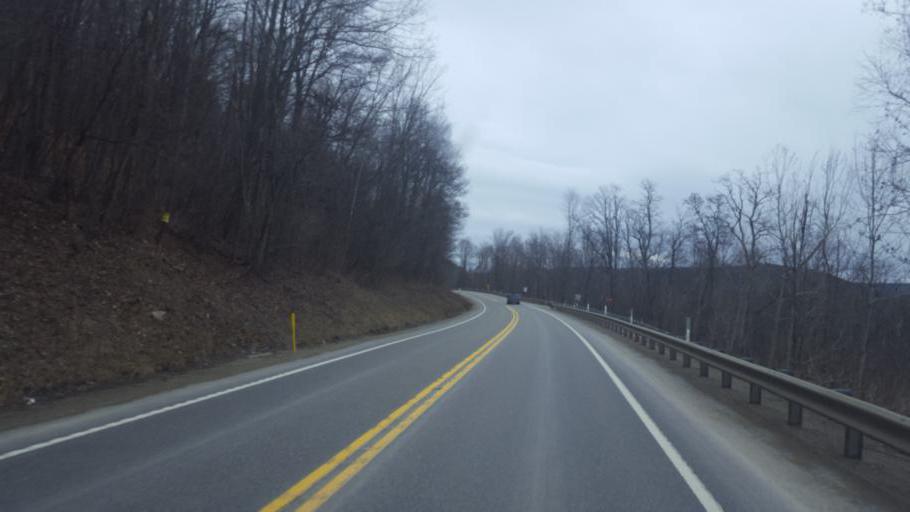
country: US
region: Pennsylvania
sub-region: Potter County
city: Coudersport
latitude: 41.7527
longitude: -78.1046
